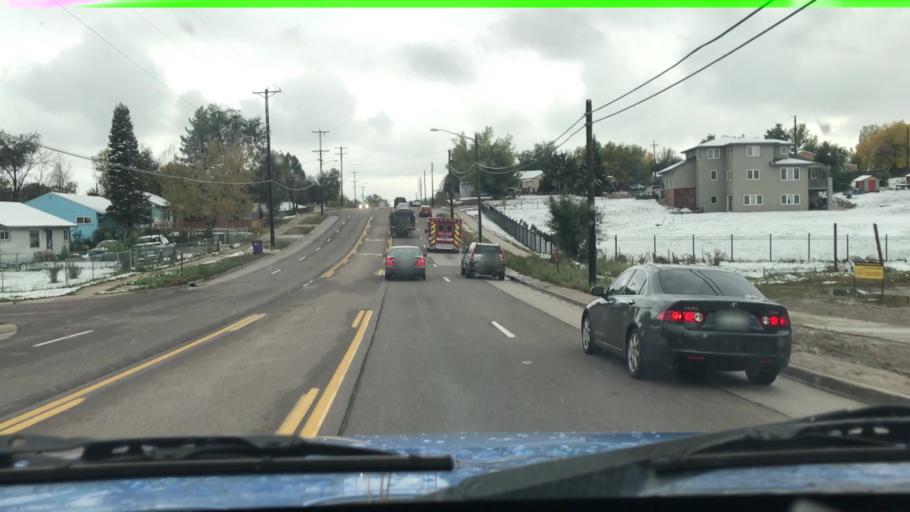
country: US
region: Colorado
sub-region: Jefferson County
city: Lakewood
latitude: 39.7088
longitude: -105.0533
